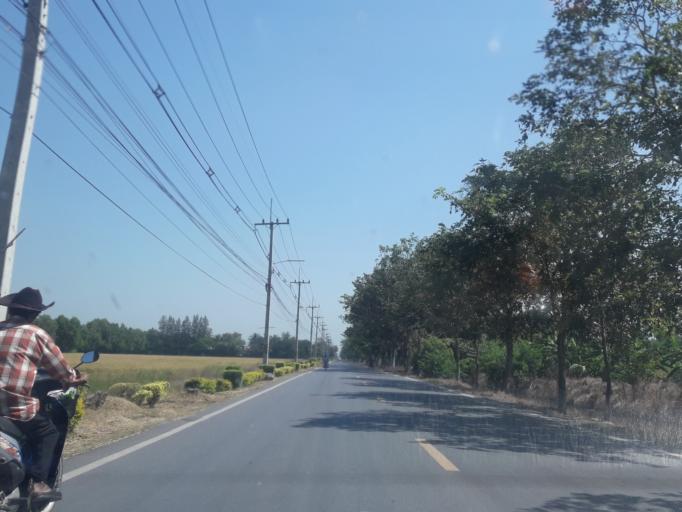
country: TH
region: Pathum Thani
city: Nong Suea
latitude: 14.1372
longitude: 100.8281
